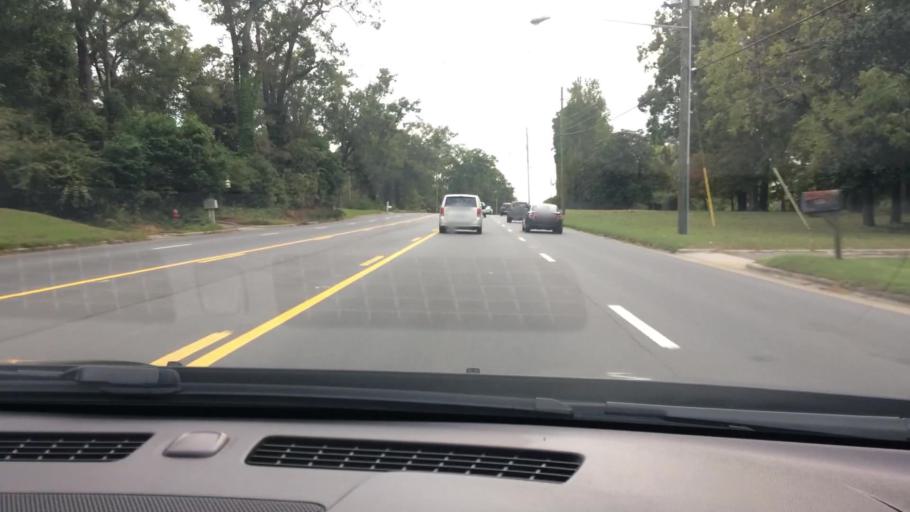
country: US
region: North Carolina
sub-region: Pitt County
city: Summerfield
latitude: 35.5843
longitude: -77.3963
